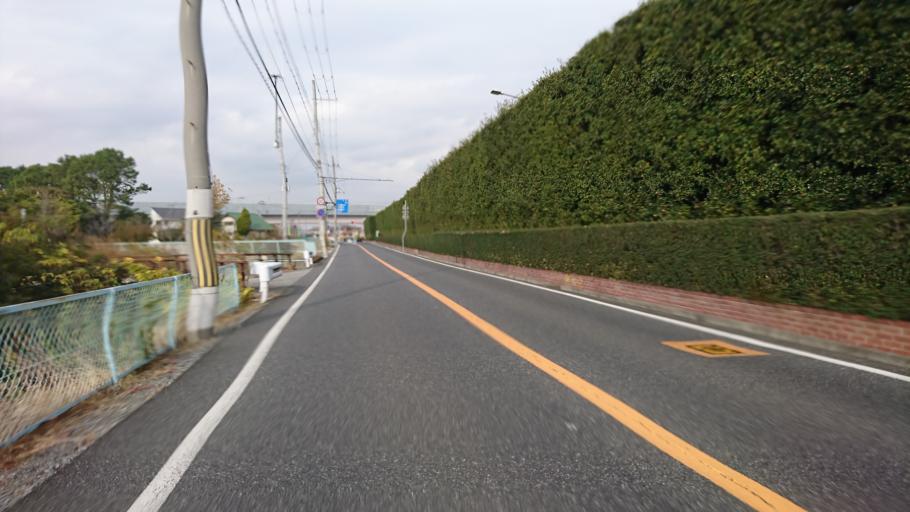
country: JP
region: Hyogo
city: Kakogawacho-honmachi
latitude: 34.7617
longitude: 134.8576
